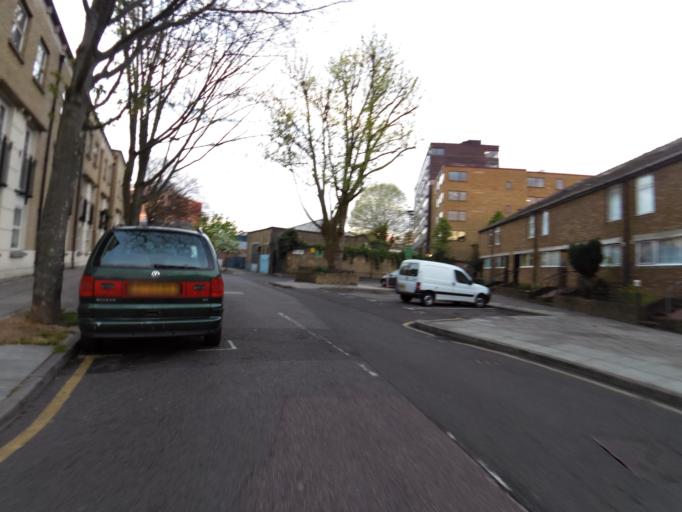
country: GB
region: England
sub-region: Greater London
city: Clerkenwell
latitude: 51.5271
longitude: -0.1159
